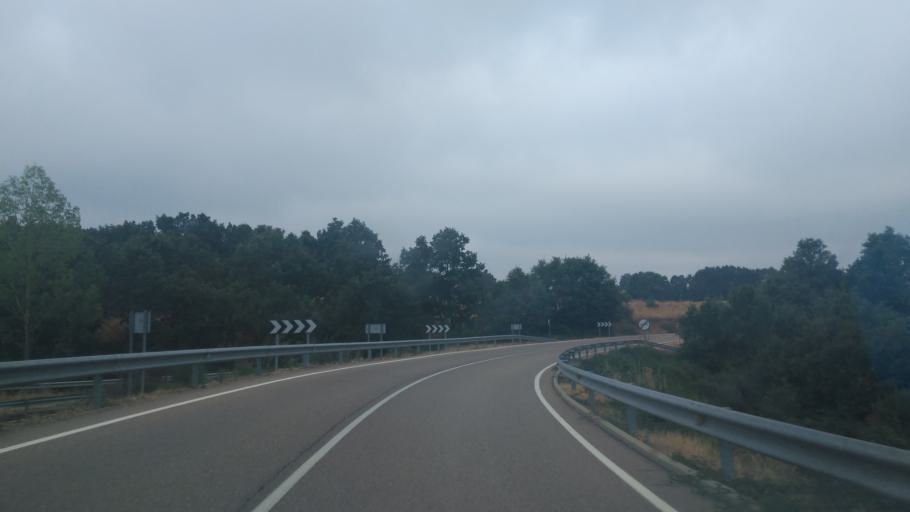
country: ES
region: Castille and Leon
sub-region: Provincia de Salamanca
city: Cereceda de la Sierra
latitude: 40.5667
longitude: -6.1115
